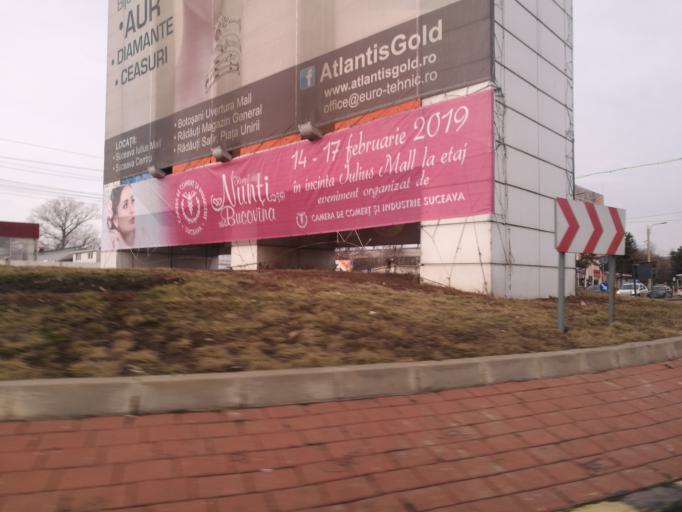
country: RO
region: Suceava
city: Suceava
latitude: 47.6600
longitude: 26.2655
